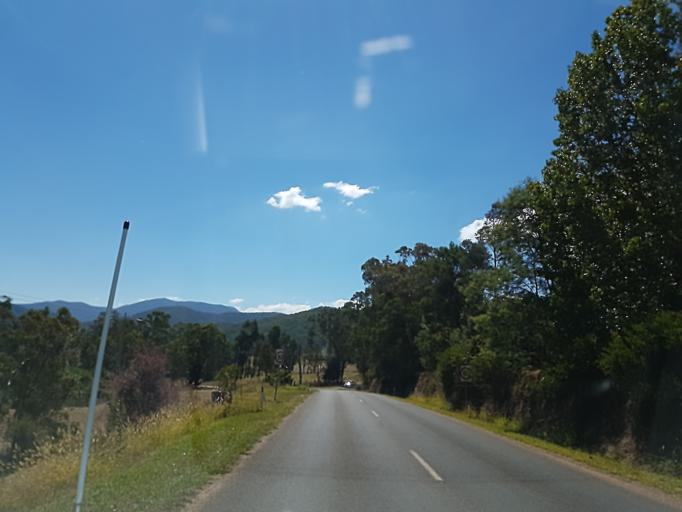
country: AU
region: Victoria
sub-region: Alpine
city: Mount Beauty
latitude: -36.7566
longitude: 146.9831
